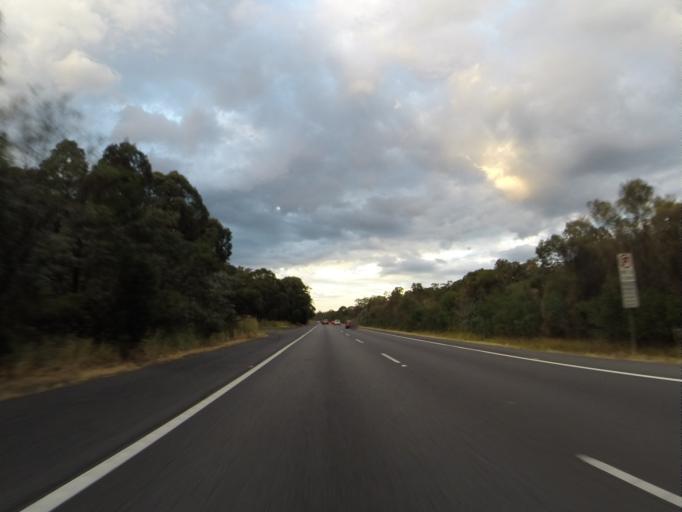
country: AU
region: New South Wales
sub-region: Wollondilly
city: Douglas Park
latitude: -34.2043
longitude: 150.6989
